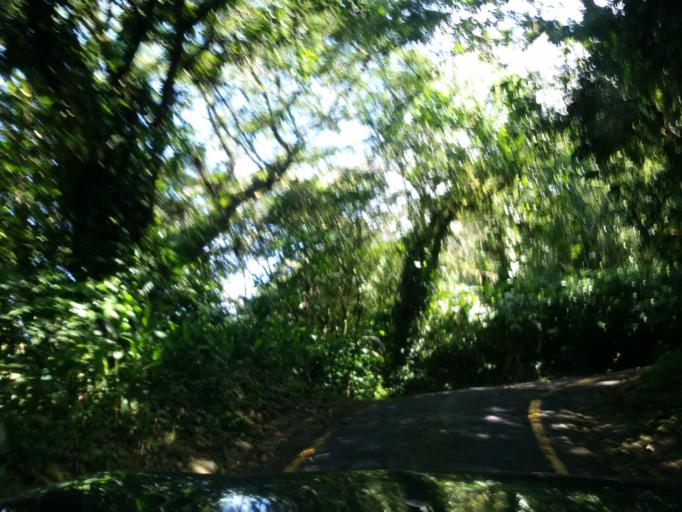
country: NI
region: Granada
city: Diriomo
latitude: 11.8377
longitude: -85.9833
